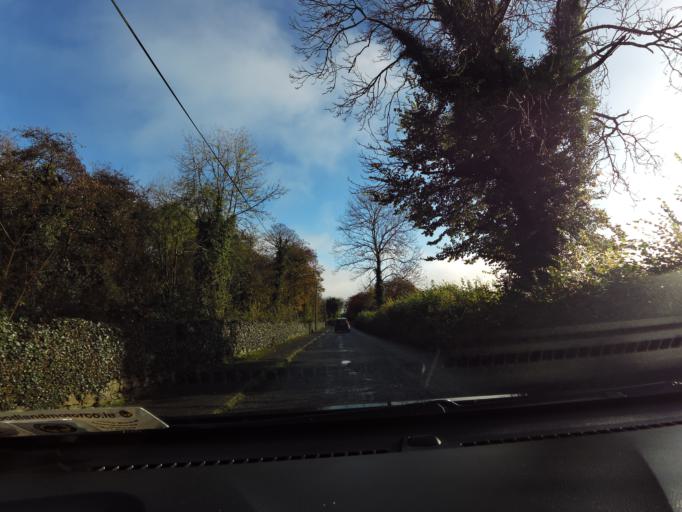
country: IE
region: Leinster
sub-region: An Iarmhi
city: Moate
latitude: 53.3749
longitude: -7.8026
